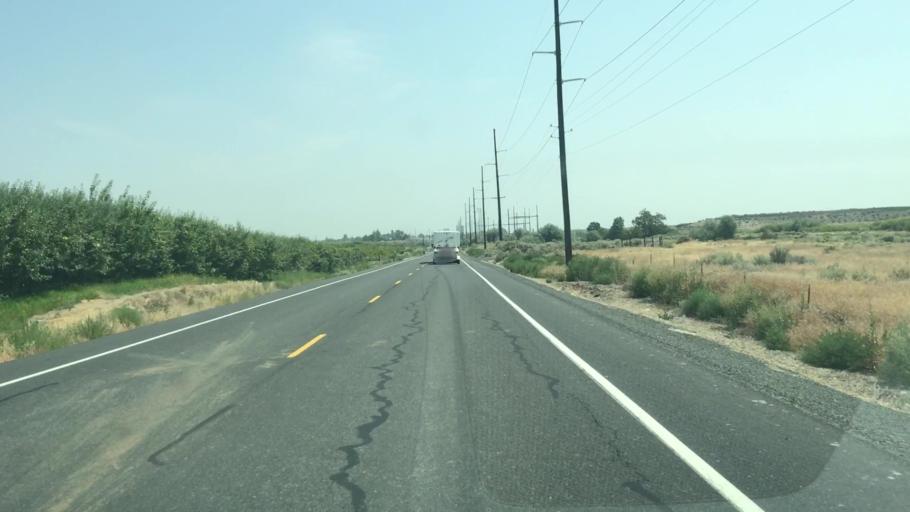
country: US
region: Washington
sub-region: Grant County
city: Quincy
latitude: 47.1601
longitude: -119.9060
